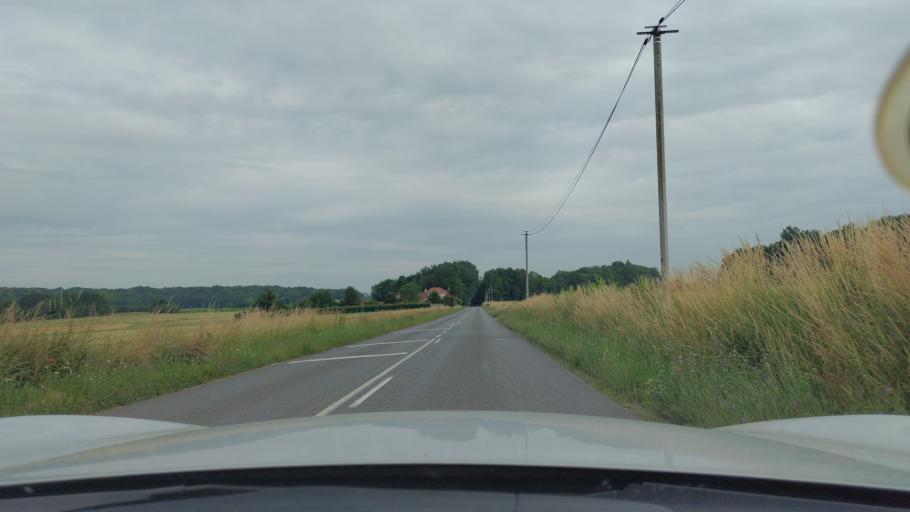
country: FR
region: Ile-de-France
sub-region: Departement de Seine-et-Marne
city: Cregy-les-Meaux
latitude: 48.9927
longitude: 2.8775
